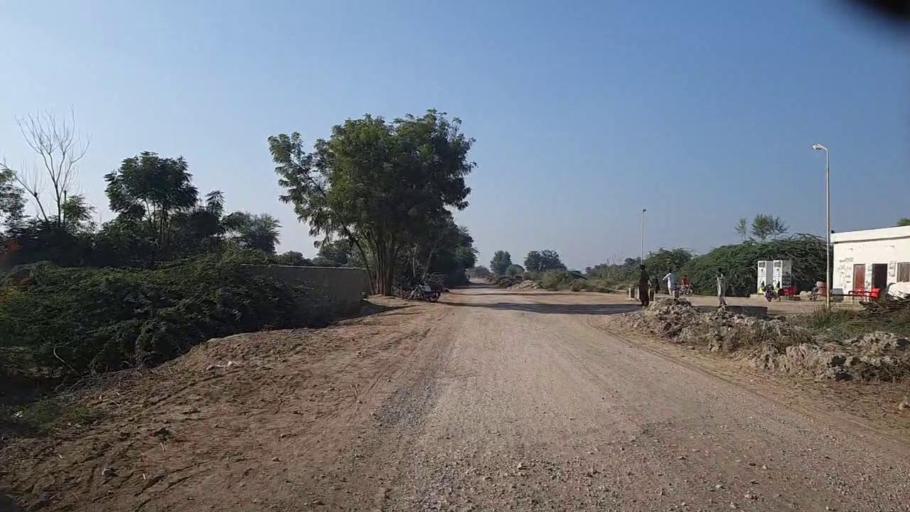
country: PK
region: Sindh
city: Darya Khan Marri
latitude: 26.6795
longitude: 68.3699
